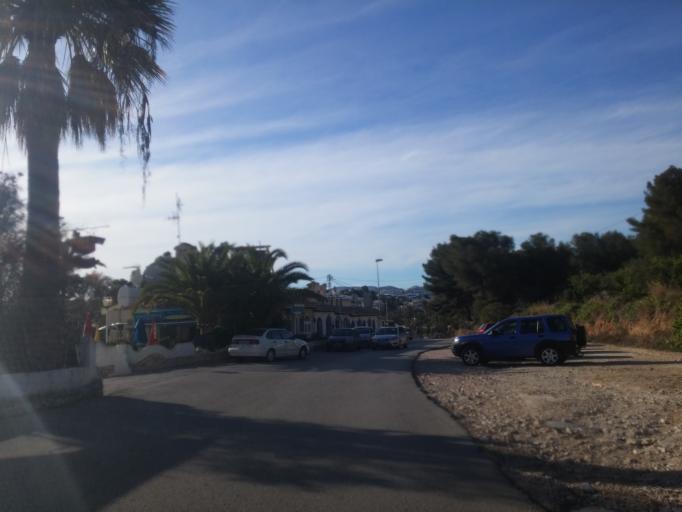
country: ES
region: Valencia
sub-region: Provincia de Alicante
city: Moraira
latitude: 38.7013
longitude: 0.1365
